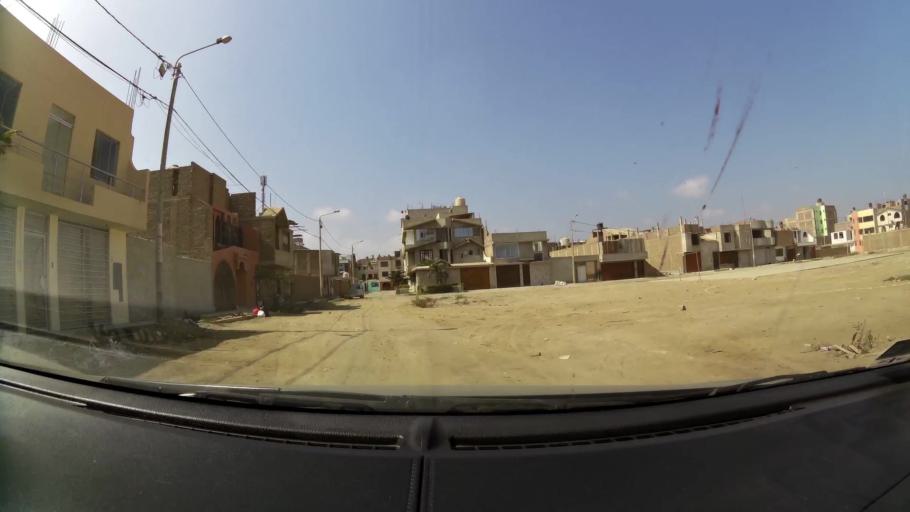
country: PE
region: La Libertad
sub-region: Provincia de Trujillo
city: Buenos Aires
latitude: -8.1370
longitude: -79.0521
